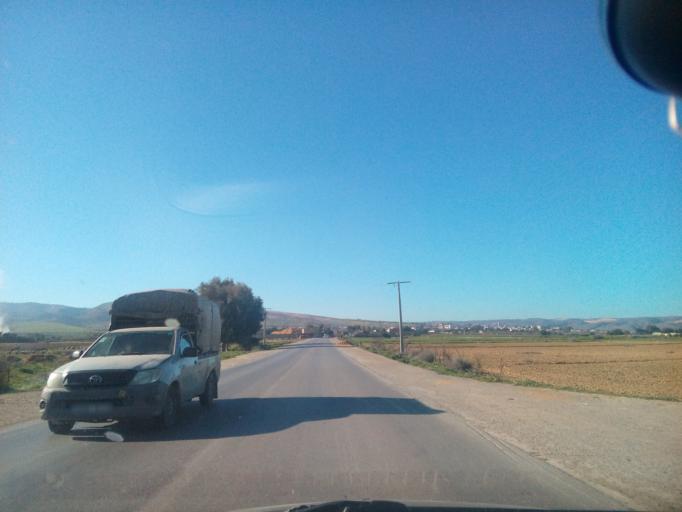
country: DZ
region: Relizane
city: Relizane
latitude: 35.8991
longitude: 0.5362
